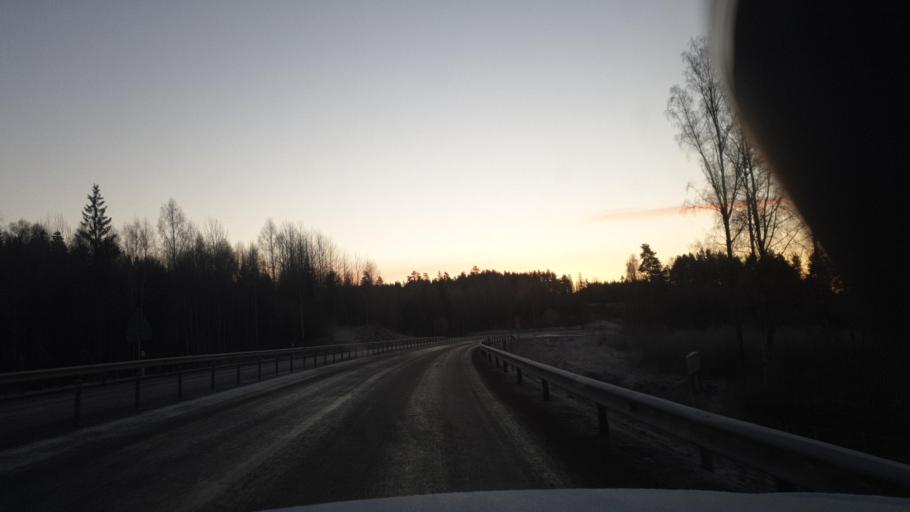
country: SE
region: Vaermland
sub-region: Arvika Kommun
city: Arvika
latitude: 59.7081
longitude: 12.5737
